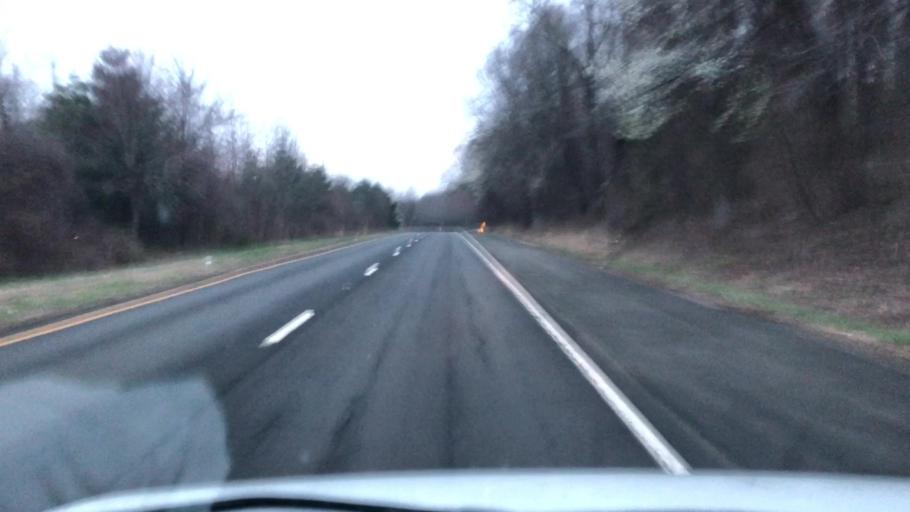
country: US
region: Maryland
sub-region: Prince George's County
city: Upper Marlboro
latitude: 38.8134
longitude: -76.7250
